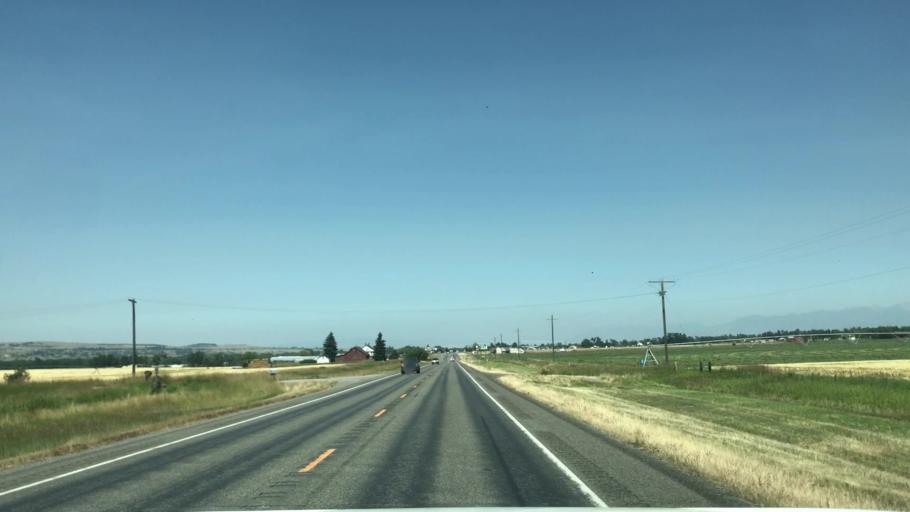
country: US
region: Montana
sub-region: Gallatin County
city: Four Corners
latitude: 45.5757
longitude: -111.1969
